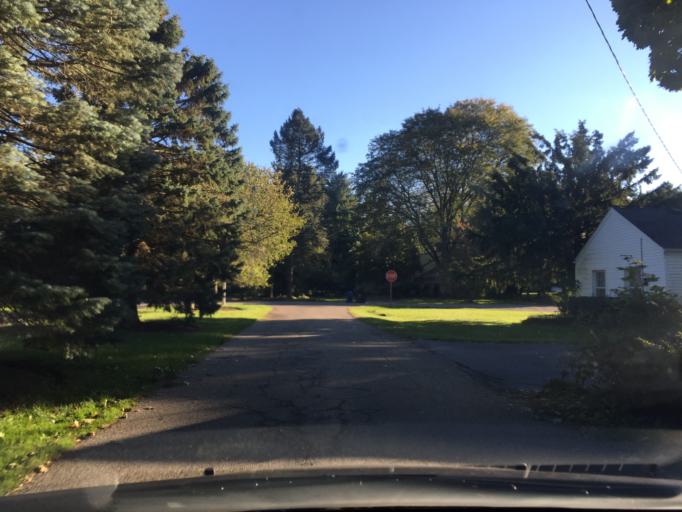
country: US
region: Michigan
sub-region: Oakland County
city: Franklin
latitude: 42.5485
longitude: -83.2905
